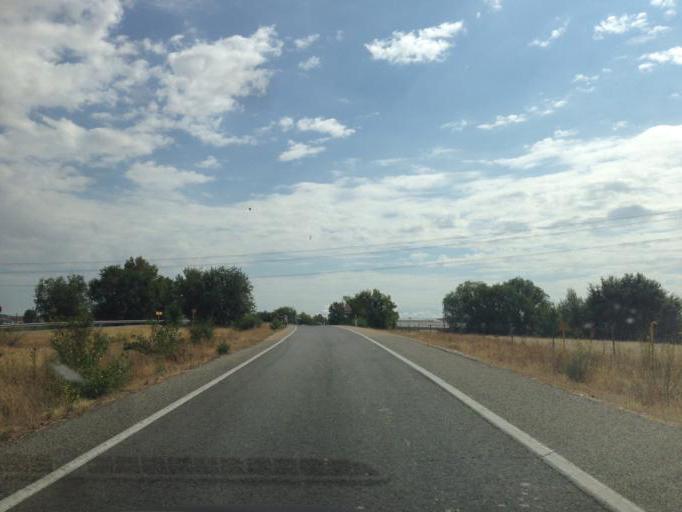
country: ES
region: Madrid
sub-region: Provincia de Madrid
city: Cobena
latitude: 40.5845
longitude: -3.5571
